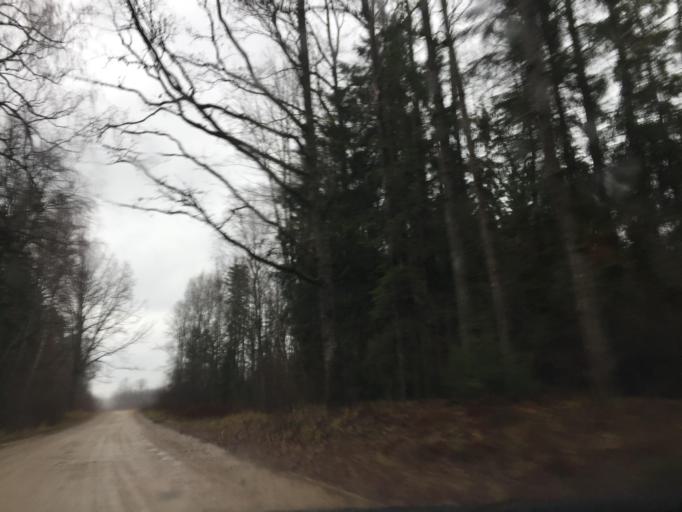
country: LV
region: Limbazu Rajons
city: Limbazi
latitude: 57.6462
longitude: 24.7754
